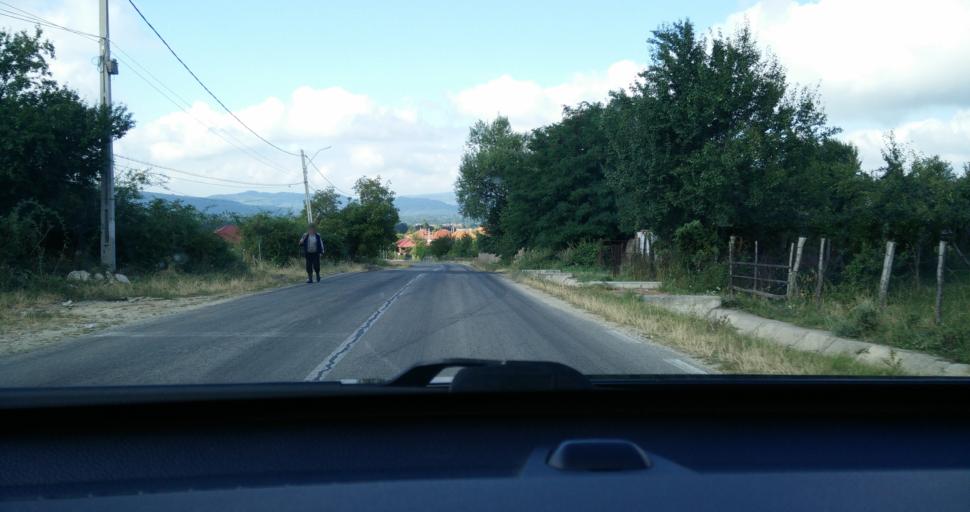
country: RO
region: Gorj
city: Novaci-Straini
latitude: 45.1798
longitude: 23.6873
